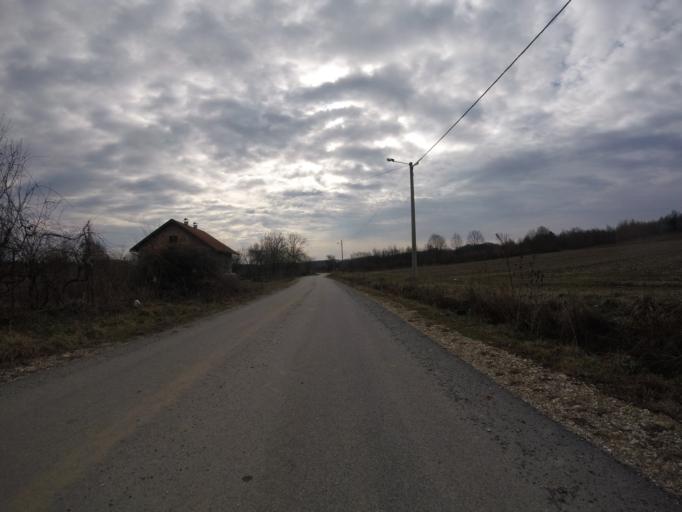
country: HR
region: Sisacko-Moslavacka
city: Glina
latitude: 45.4469
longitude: 16.0692
